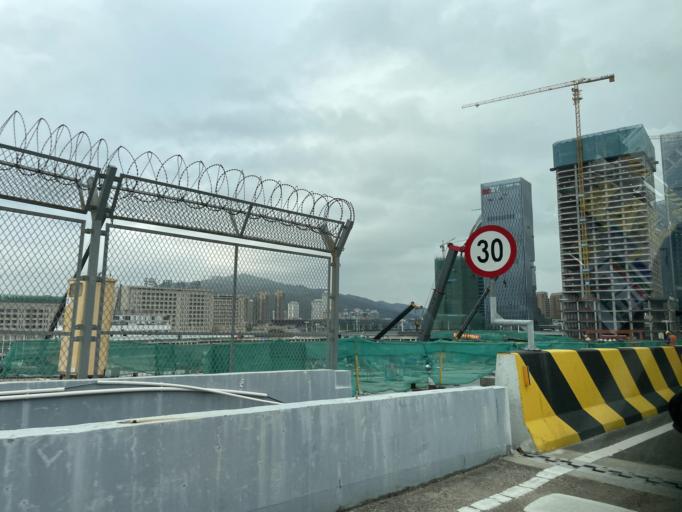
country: MO
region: Macau
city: Macau
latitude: 22.1402
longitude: 113.5471
